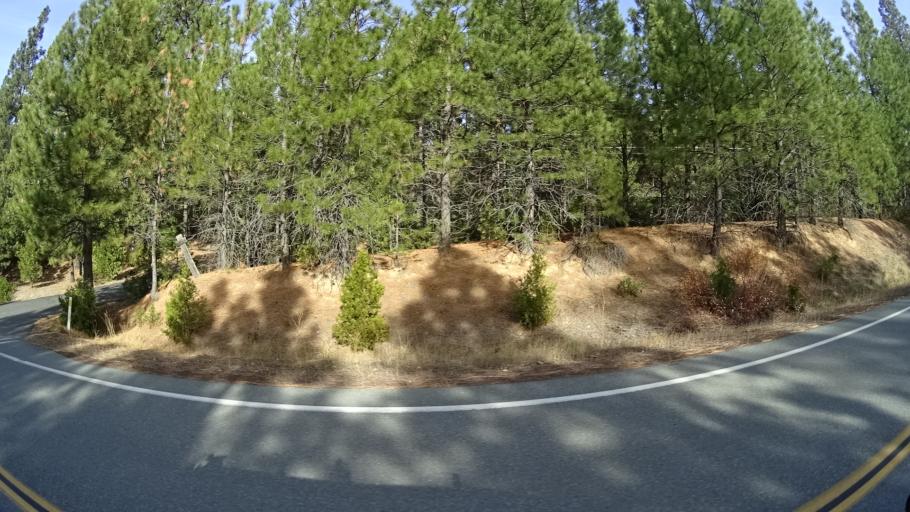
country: US
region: California
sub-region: Siskiyou County
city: Weed
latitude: 41.3902
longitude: -122.4111
